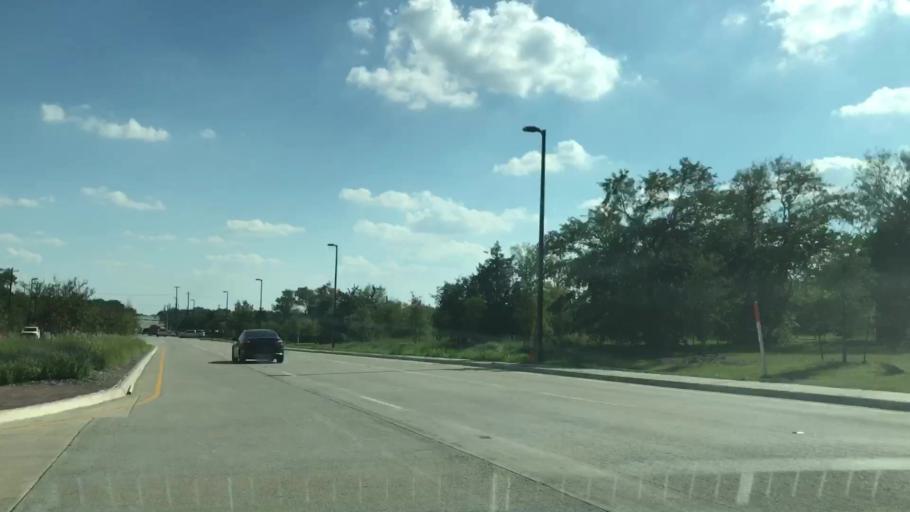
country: US
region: Texas
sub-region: Tarrant County
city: Southlake
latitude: 32.9415
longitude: -97.1860
